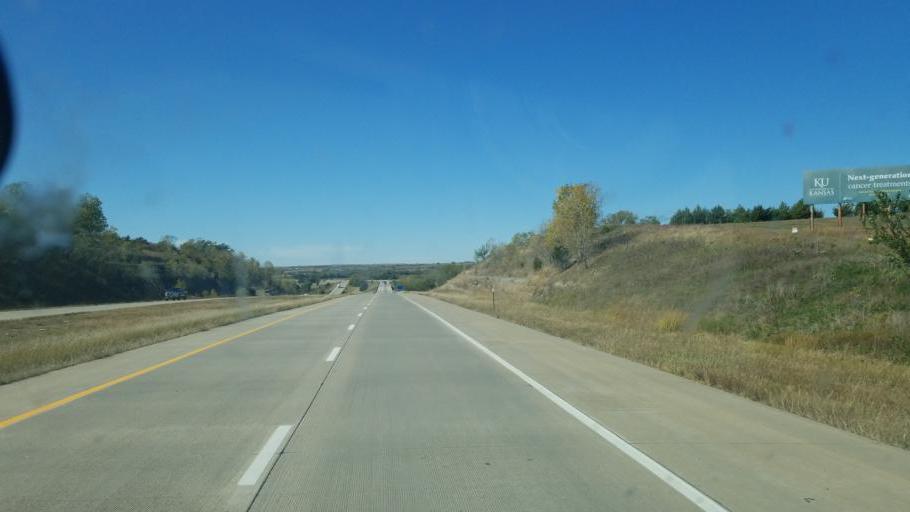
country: US
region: Kansas
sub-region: Wabaunsee County
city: Alma
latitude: 39.0600
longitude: -96.1749
